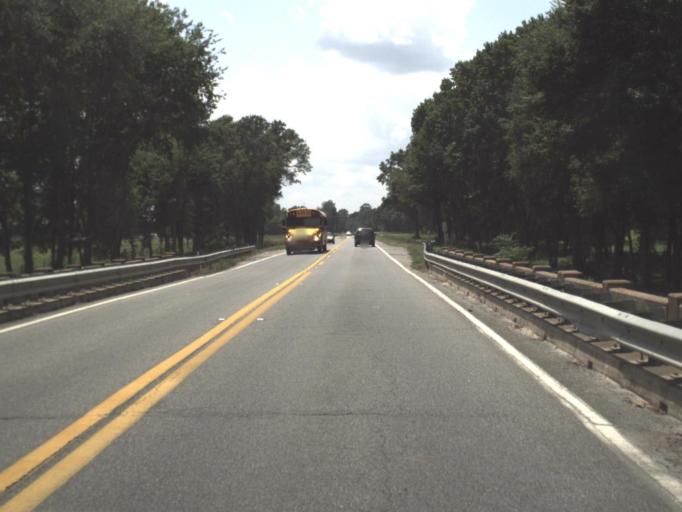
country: US
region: Florida
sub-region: Hamilton County
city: Jasper
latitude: 30.5239
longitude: -83.0152
